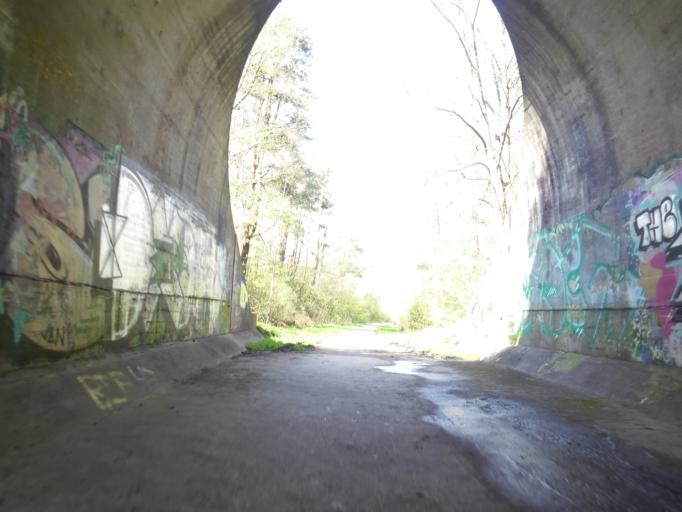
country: DK
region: Central Jutland
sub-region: Skive Kommune
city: Skive
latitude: 56.5701
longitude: 9.0065
